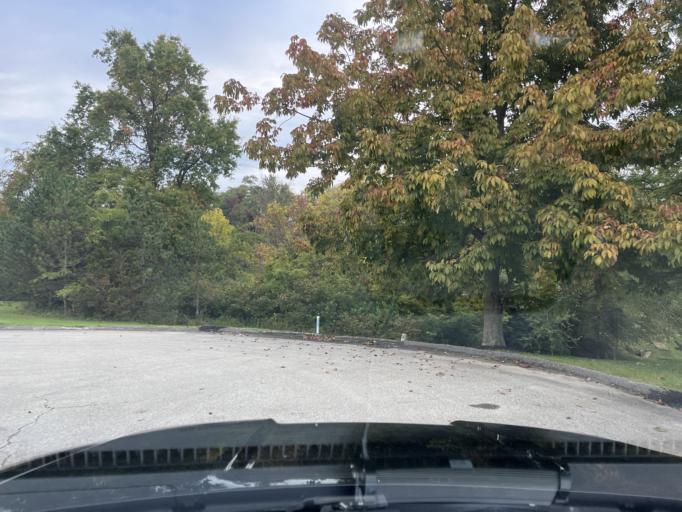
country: US
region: Pennsylvania
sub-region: Fayette County
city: Leith-Hatfield
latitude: 39.8763
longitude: -79.7318
